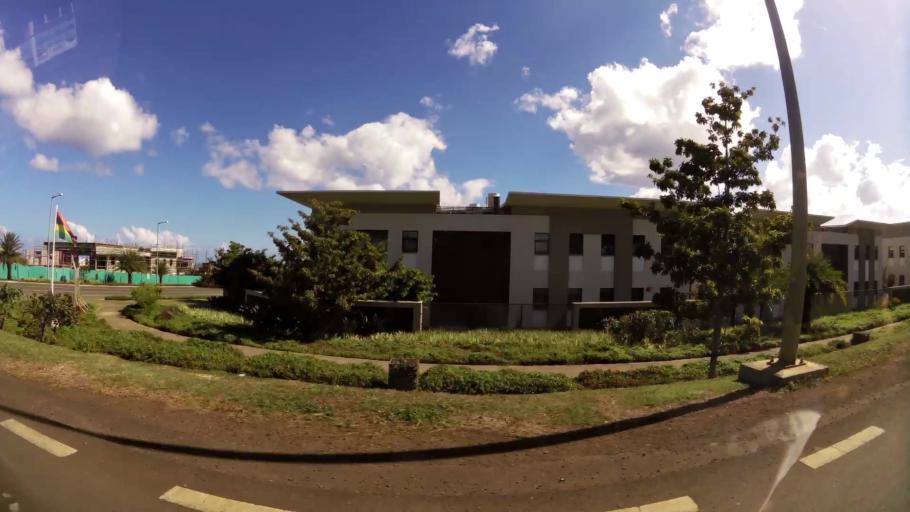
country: MU
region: Black River
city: Cascavelle
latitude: -20.2734
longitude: 57.4054
